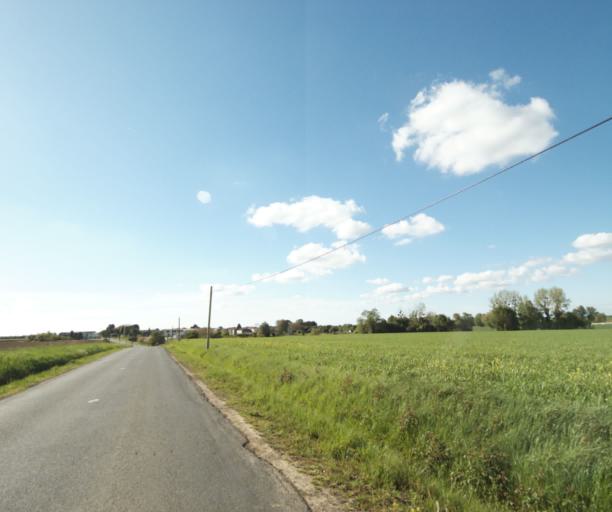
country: FR
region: Poitou-Charentes
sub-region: Departement de la Charente-Maritime
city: Corme-Royal
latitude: 45.7110
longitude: -0.8002
